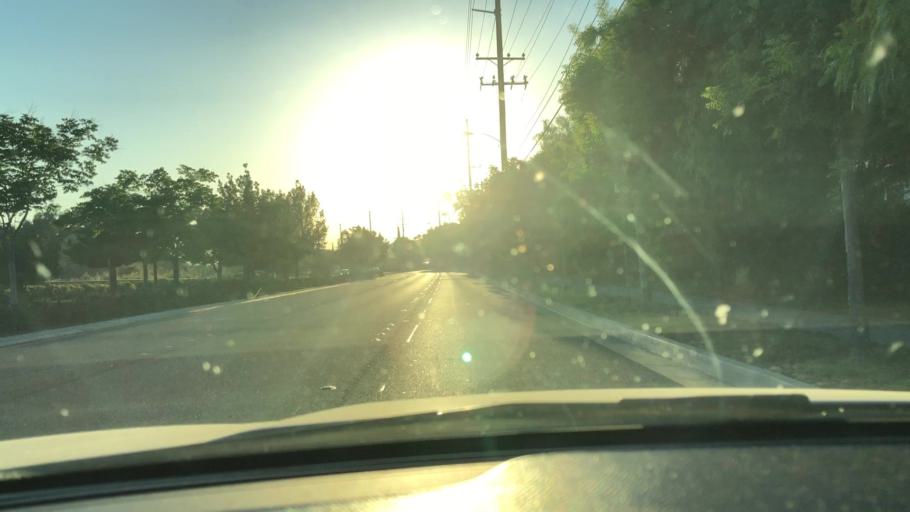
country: US
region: California
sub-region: Los Angeles County
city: Santa Clarita
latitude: 34.4210
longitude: -118.4855
